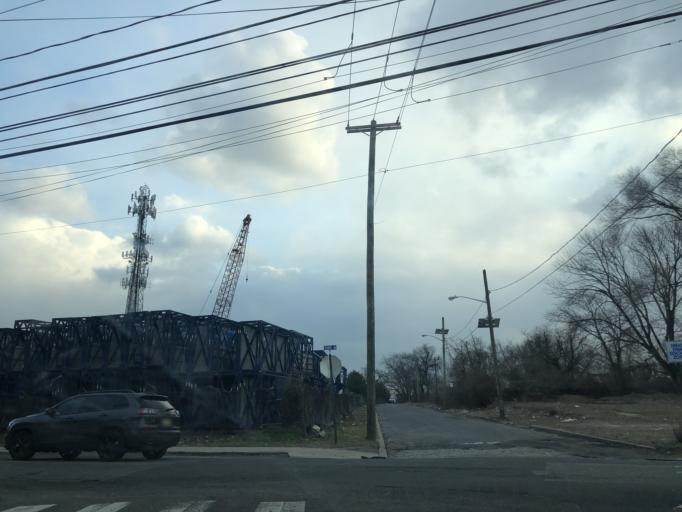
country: US
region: New Jersey
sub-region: Camden County
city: Wood-Lynne
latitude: 39.9196
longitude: -75.1078
